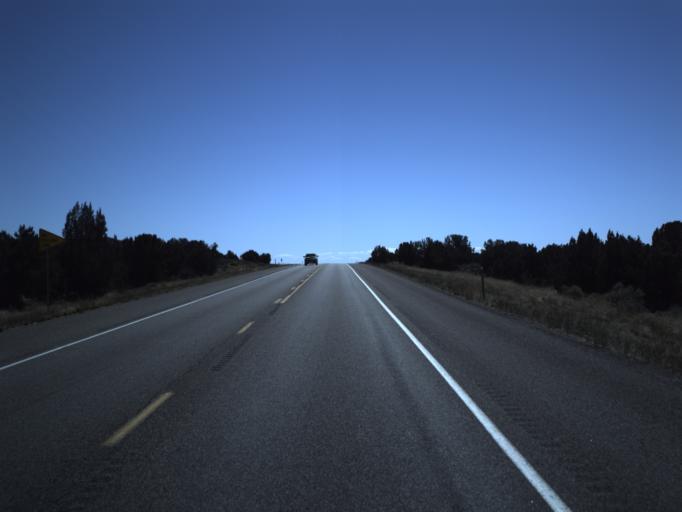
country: US
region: Utah
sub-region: Washington County
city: Ivins
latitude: 37.2906
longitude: -113.6600
